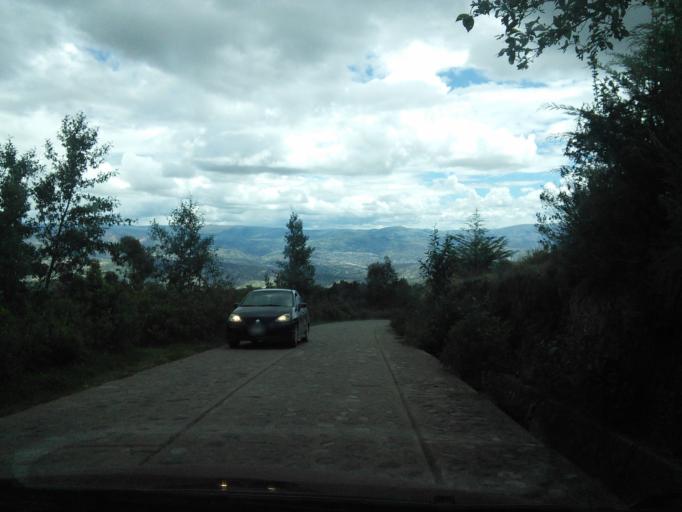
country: PE
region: Ayacucho
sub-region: Provincia de Huamanga
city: Quinua
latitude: -13.0436
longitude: -74.1313
